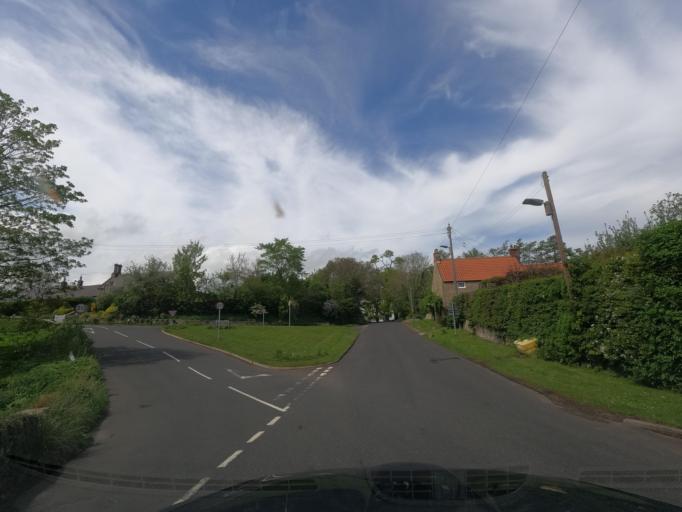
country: GB
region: England
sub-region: Northumberland
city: Whittingham
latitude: 55.4018
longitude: -1.8914
